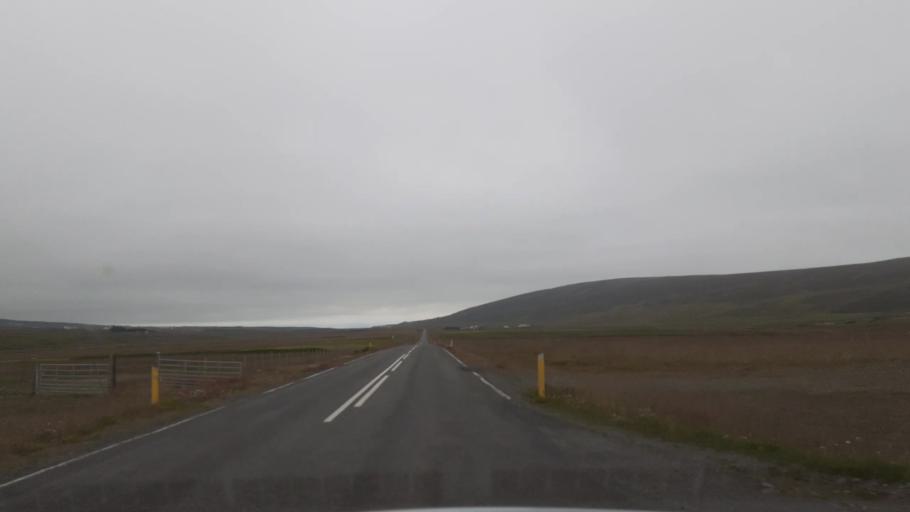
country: IS
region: Northeast
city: Siglufjoerdur
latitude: 65.7409
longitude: -19.1423
